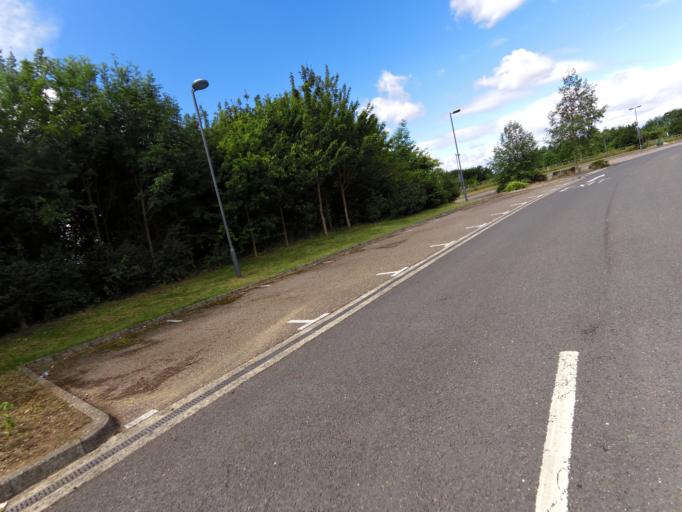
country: GB
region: England
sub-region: Cambridgeshire
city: Grantchester
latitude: 52.1665
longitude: 0.1066
